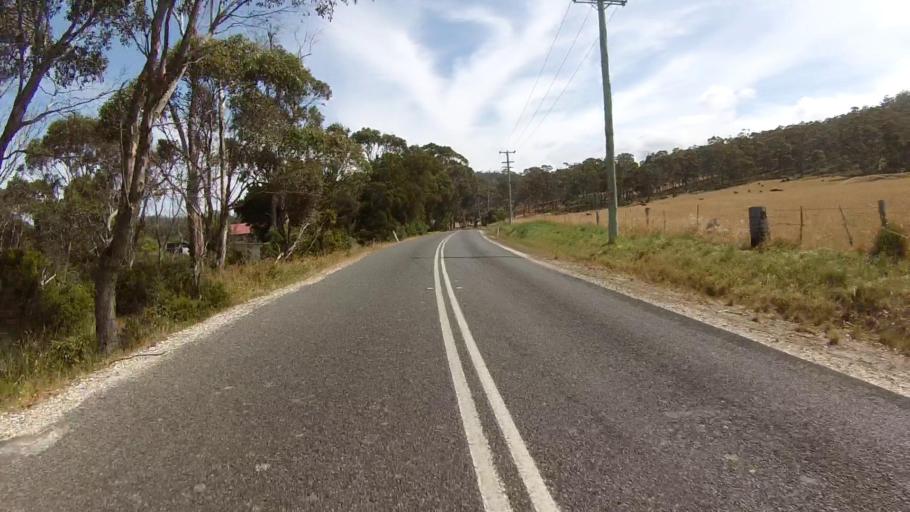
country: AU
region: Tasmania
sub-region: Huon Valley
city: Cygnet
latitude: -43.2779
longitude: 147.1630
